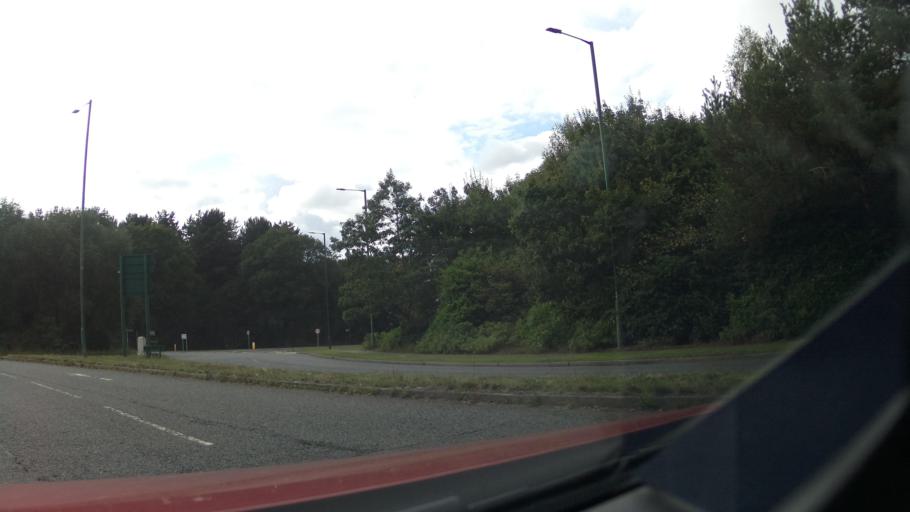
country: GB
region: England
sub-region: Solihull
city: Chelmsley Wood
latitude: 52.4627
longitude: -1.7216
